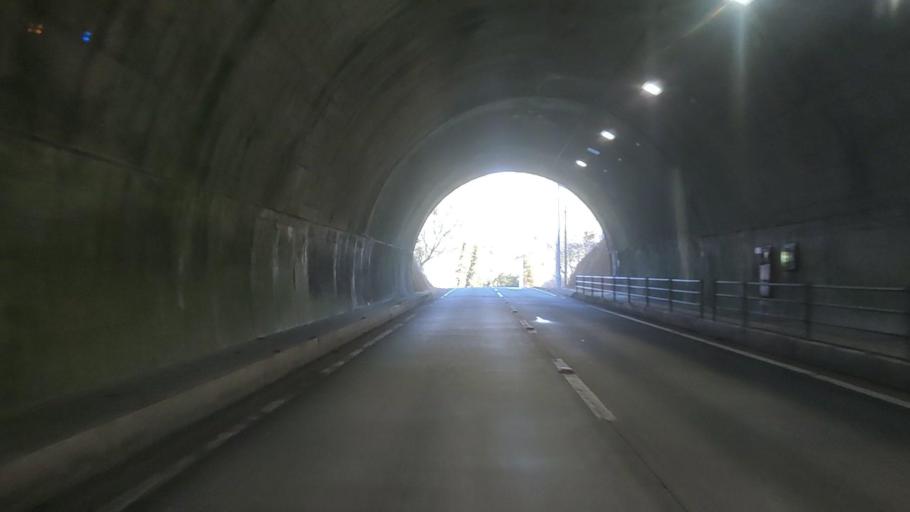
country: JP
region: Miyazaki
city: Nobeoka
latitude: 32.7394
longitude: 131.8245
